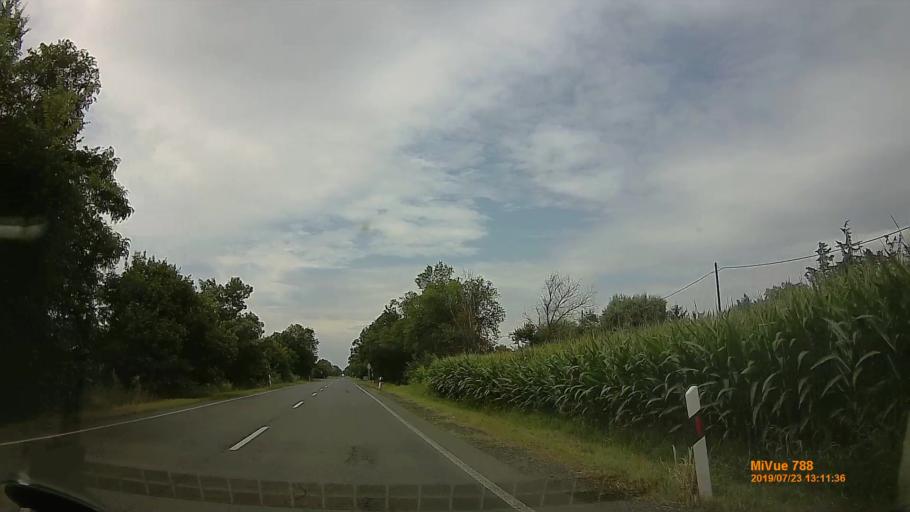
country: HU
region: Szabolcs-Szatmar-Bereg
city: Tiszavasvari
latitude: 47.9285
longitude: 21.2688
